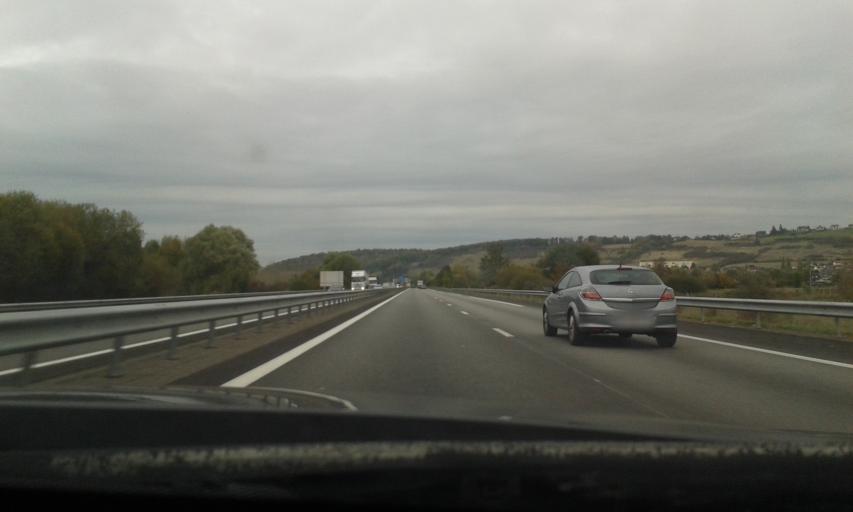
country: FR
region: Haute-Normandie
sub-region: Departement de l'Eure
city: Louviers
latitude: 49.1983
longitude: 1.1748
